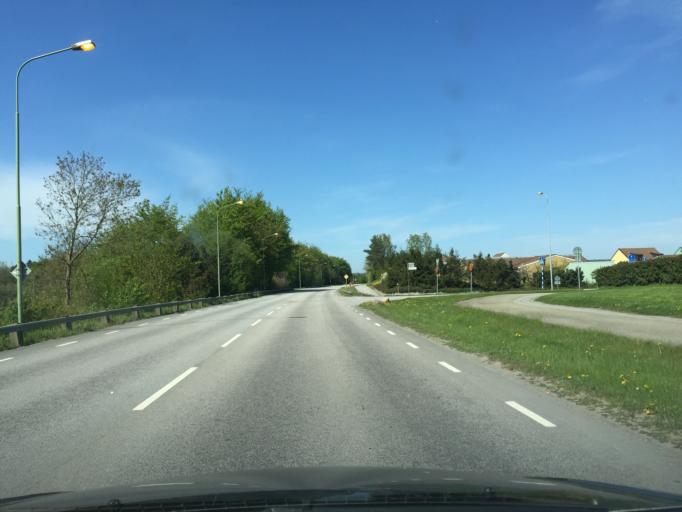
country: SE
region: Skane
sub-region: Skurups Kommun
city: Skurup
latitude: 55.4844
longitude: 13.5031
